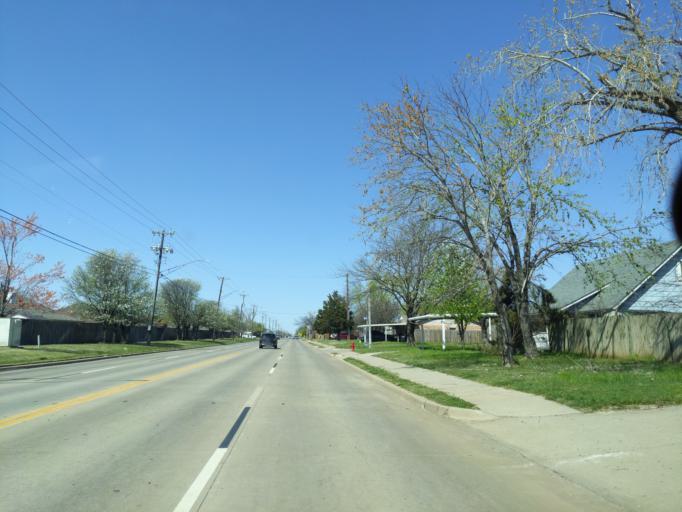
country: US
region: Oklahoma
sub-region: Cleveland County
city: Moore
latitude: 35.3360
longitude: -97.5120
